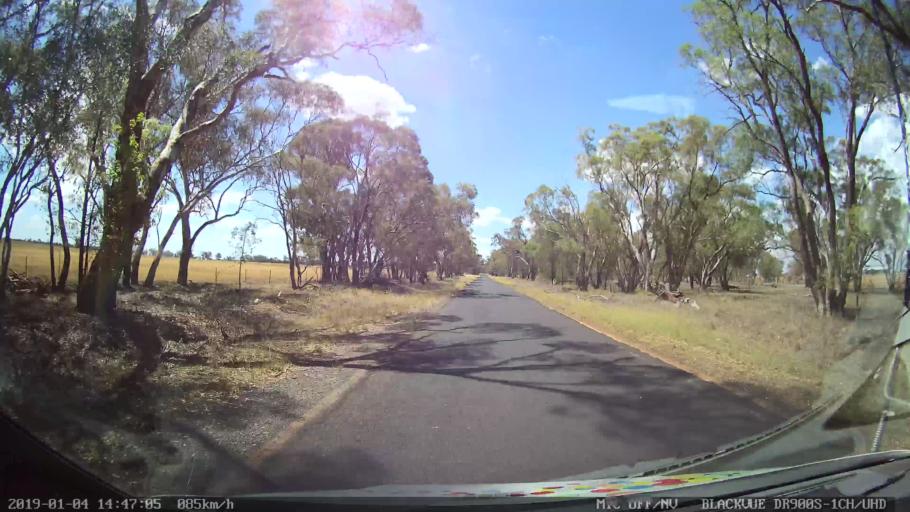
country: AU
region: New South Wales
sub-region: Dubbo Municipality
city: Dubbo
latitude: -32.0734
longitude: 148.6595
